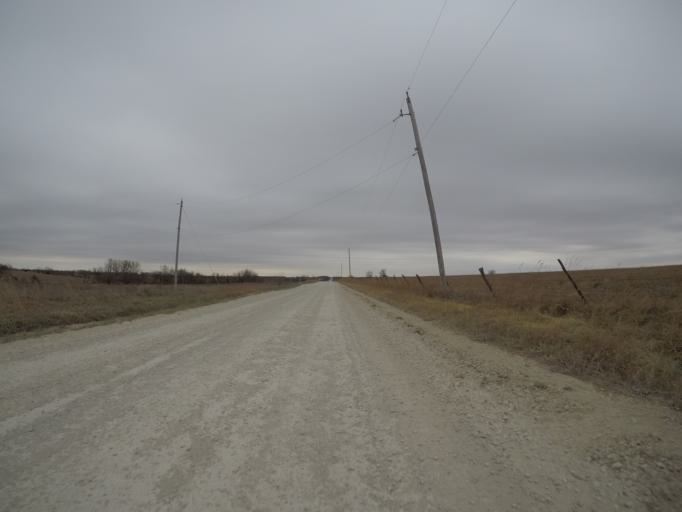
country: US
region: Kansas
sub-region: Wabaunsee County
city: Alma
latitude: 38.8213
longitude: -96.1133
